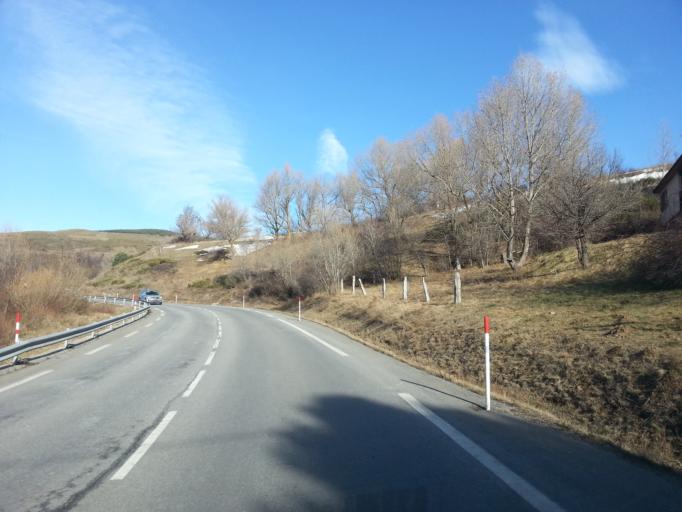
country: ES
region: Catalonia
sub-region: Provincia de Girona
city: Llivia
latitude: 42.4654
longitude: 2.0344
